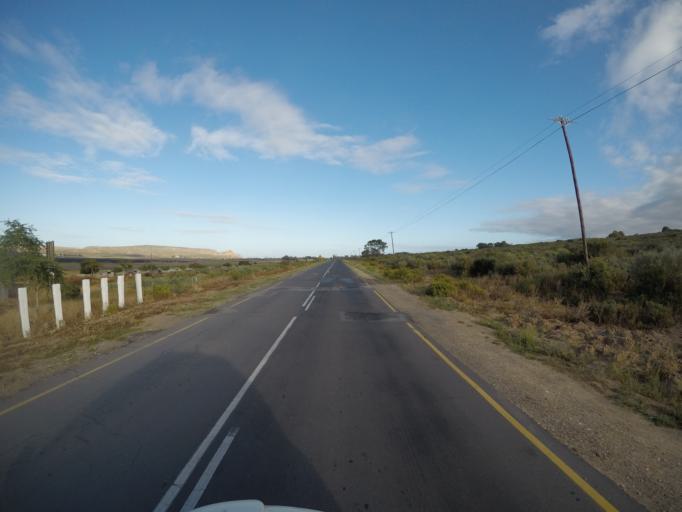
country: ZA
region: Western Cape
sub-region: West Coast District Municipality
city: Clanwilliam
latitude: -32.3143
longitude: 18.3955
